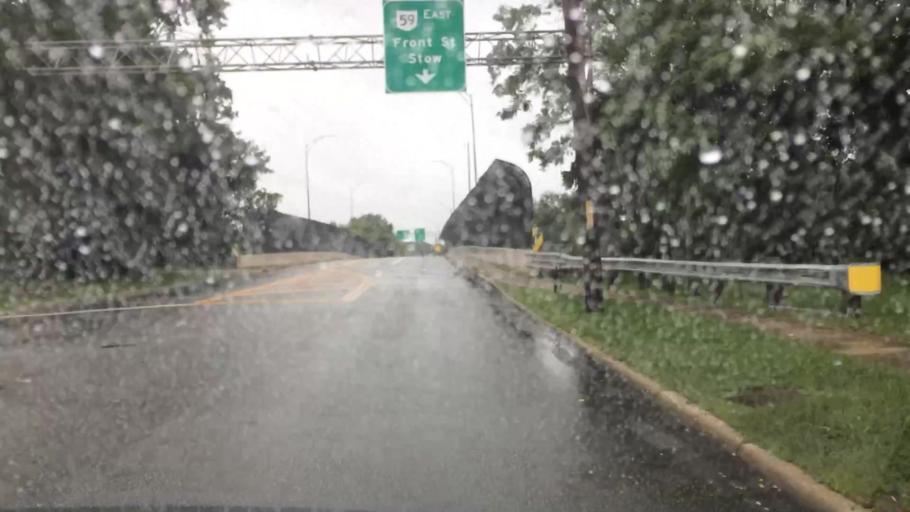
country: US
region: Ohio
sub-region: Summit County
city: Cuyahoga Falls
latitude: 41.1416
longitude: -81.4786
